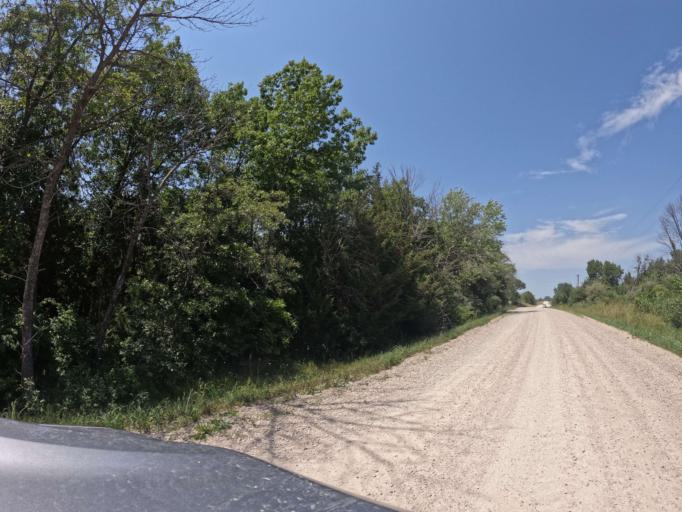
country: US
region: Iowa
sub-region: Henry County
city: Mount Pleasant
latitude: 40.8925
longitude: -91.6891
